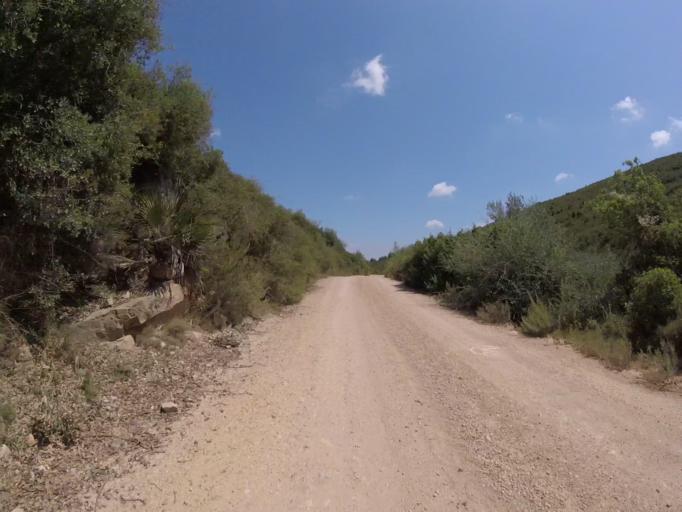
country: ES
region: Valencia
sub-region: Provincia de Castello
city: Torreblanca
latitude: 40.2265
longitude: 0.1557
